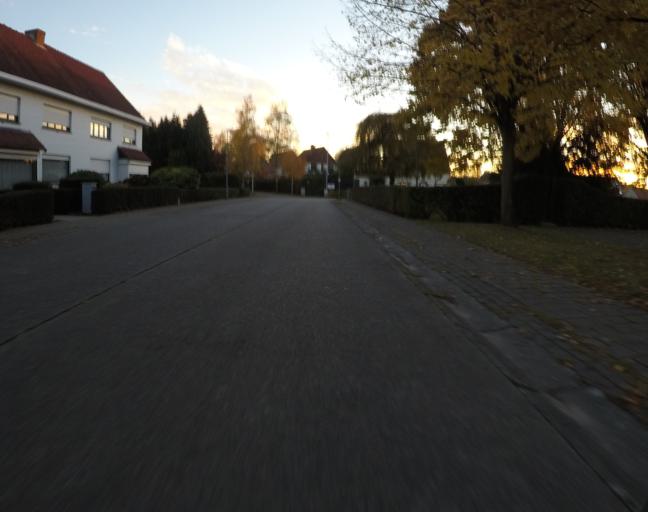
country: BE
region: Flanders
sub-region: Provincie Antwerpen
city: Herentals
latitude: 51.1655
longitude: 4.8312
